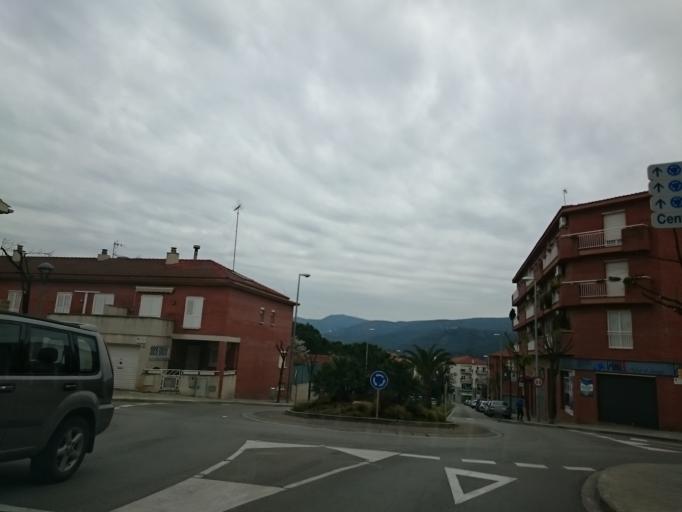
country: ES
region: Catalonia
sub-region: Provincia de Barcelona
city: Sant Sadurni d'Anoia
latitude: 41.4275
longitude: 1.7877
